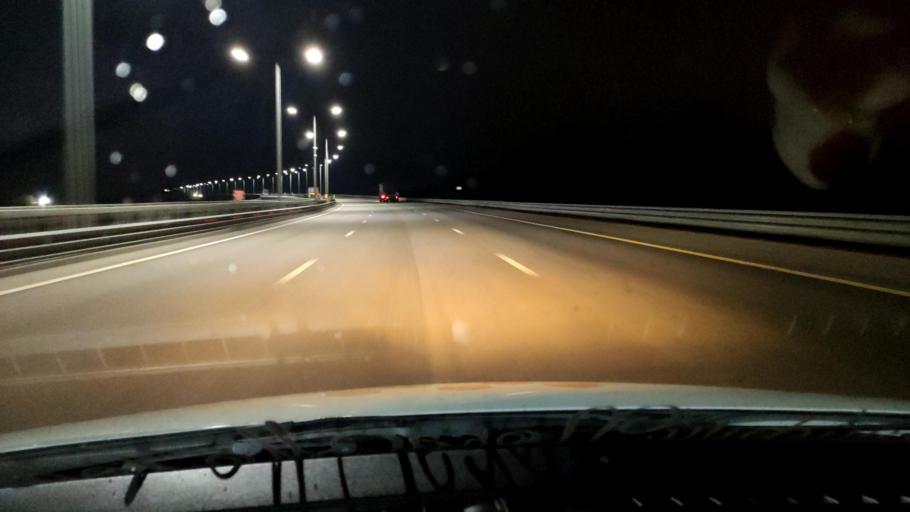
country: RU
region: Voronezj
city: Somovo
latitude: 51.7973
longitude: 39.2575
